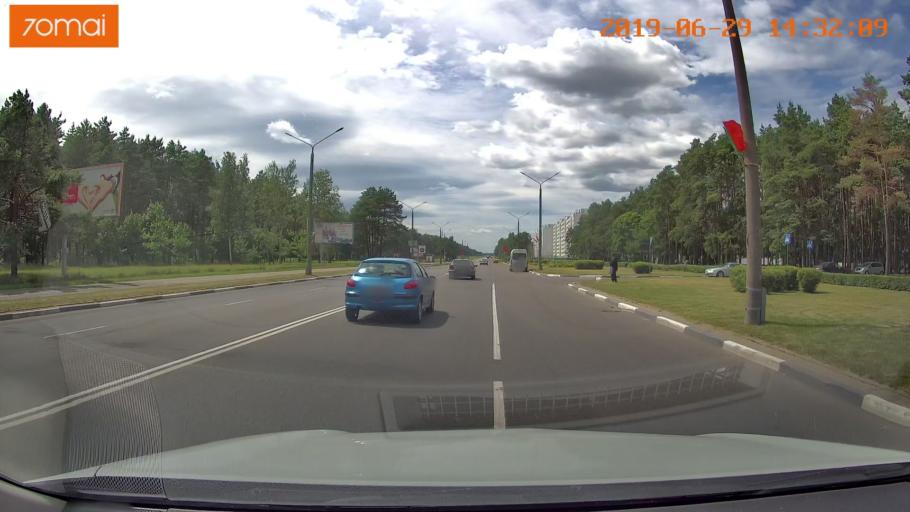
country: BY
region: Minsk
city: Salihorsk
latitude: 52.7815
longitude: 27.5059
